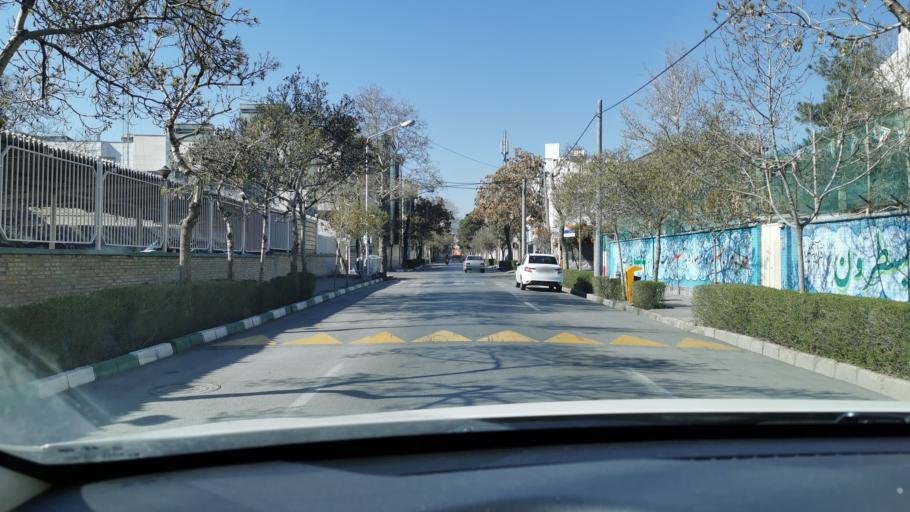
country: IR
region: Razavi Khorasan
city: Mashhad
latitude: 36.2888
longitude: 59.5867
